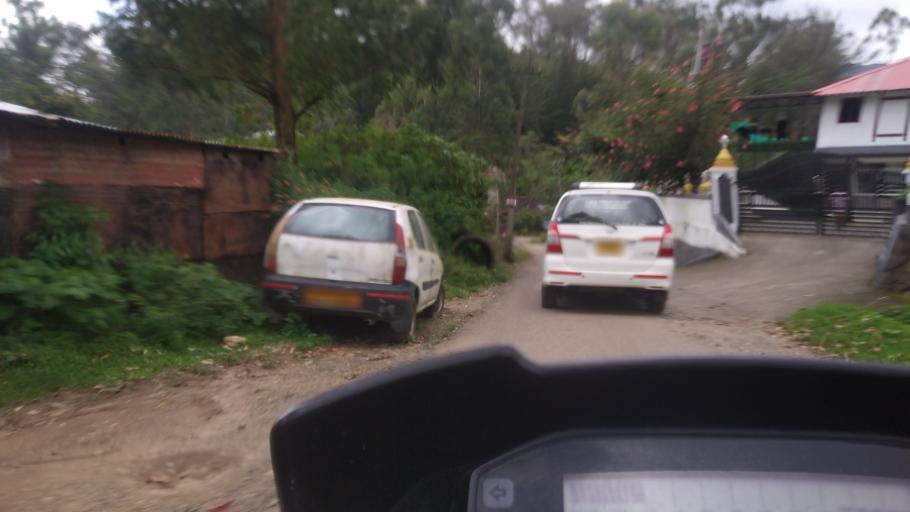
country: IN
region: Kerala
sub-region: Idukki
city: Munnar
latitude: 10.0647
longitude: 77.1077
